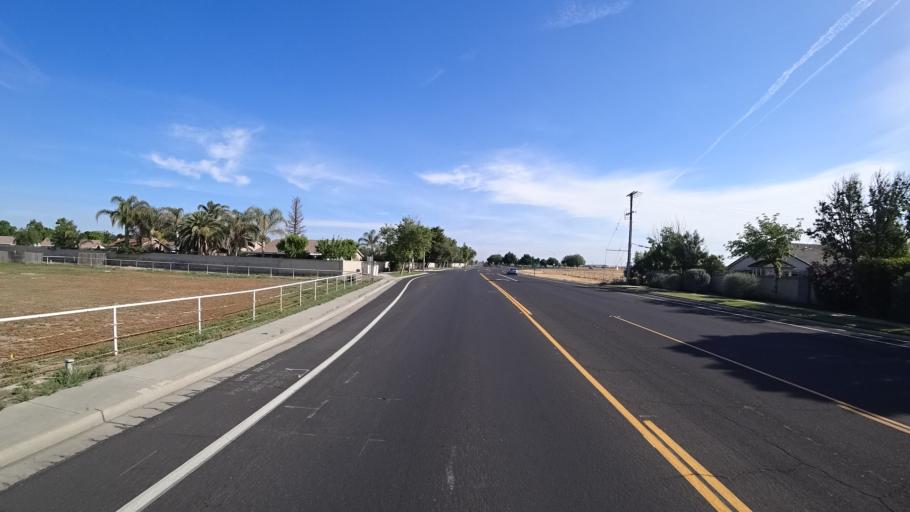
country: US
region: California
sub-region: Kings County
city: Lucerne
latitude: 36.3644
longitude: -119.6371
